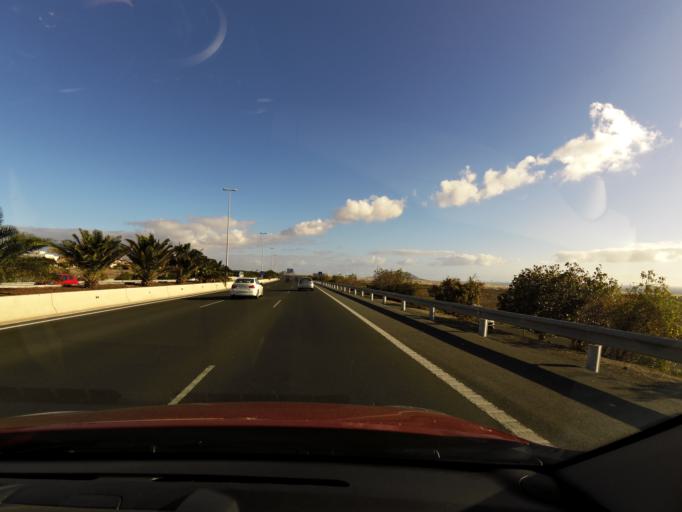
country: ES
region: Canary Islands
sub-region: Provincia de Las Palmas
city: Cruce de Arinaga
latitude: 27.8325
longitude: -15.4441
